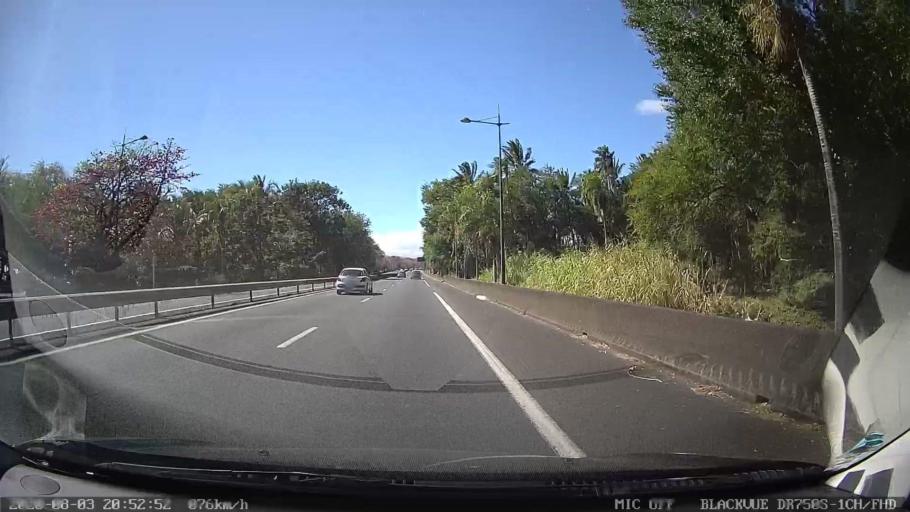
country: RE
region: Reunion
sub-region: Reunion
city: Saint-Denis
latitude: -20.8862
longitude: 55.4926
